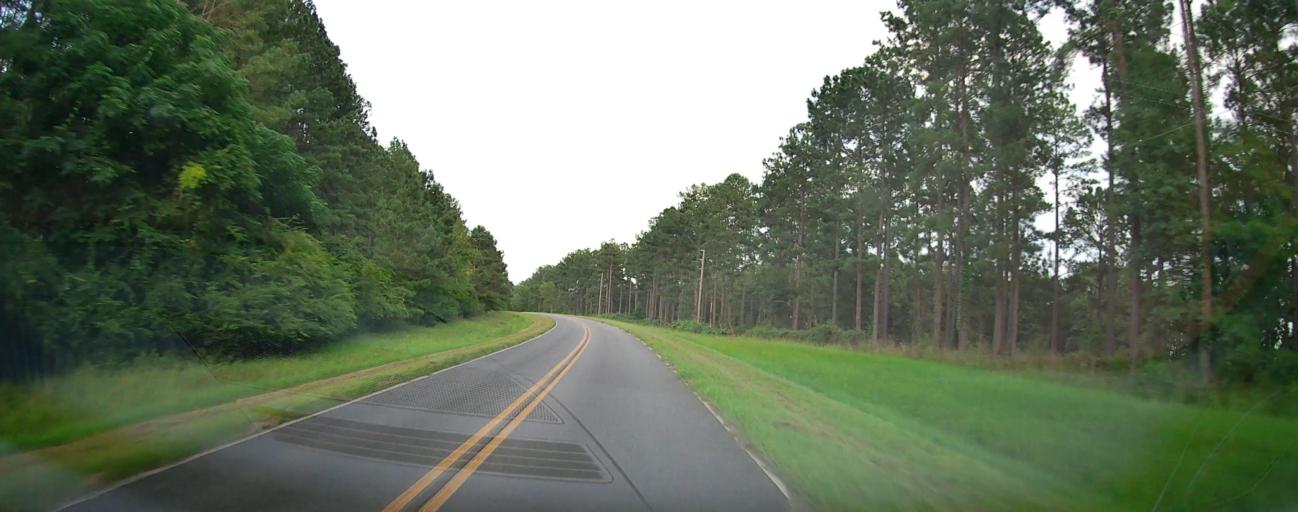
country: US
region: Georgia
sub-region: Crawford County
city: Roberta
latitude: 32.6582
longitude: -84.0603
